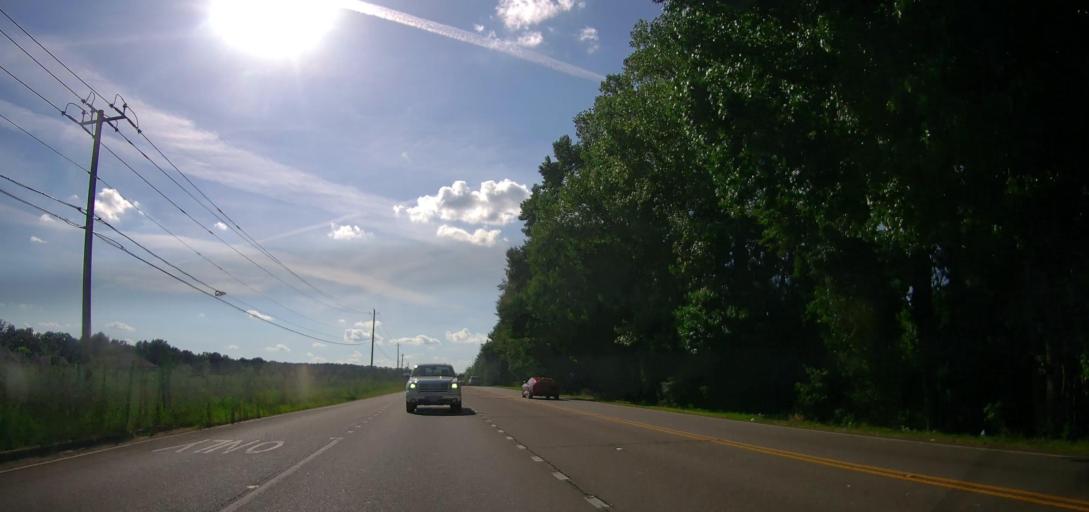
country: US
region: Alabama
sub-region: Tuscaloosa County
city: Holt
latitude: 33.1905
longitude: -87.4616
